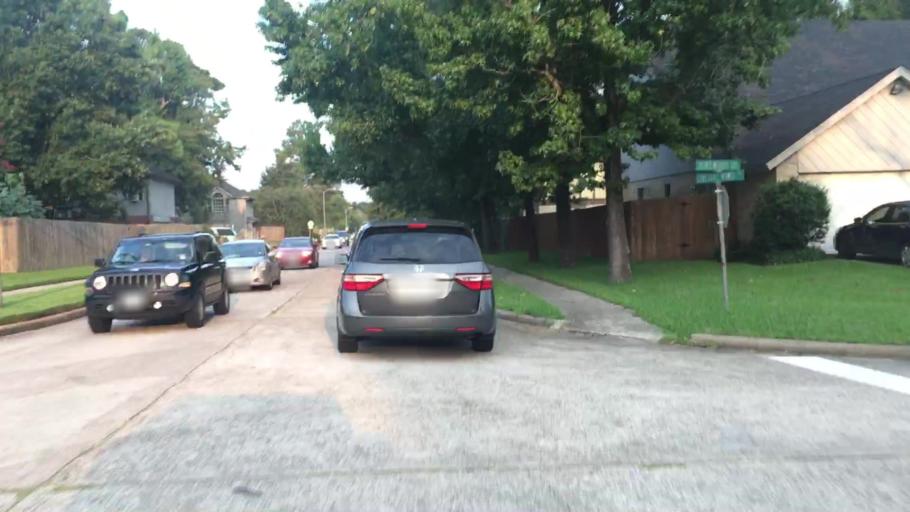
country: US
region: Texas
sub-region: Harris County
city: Atascocita
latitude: 29.9925
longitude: -95.1629
